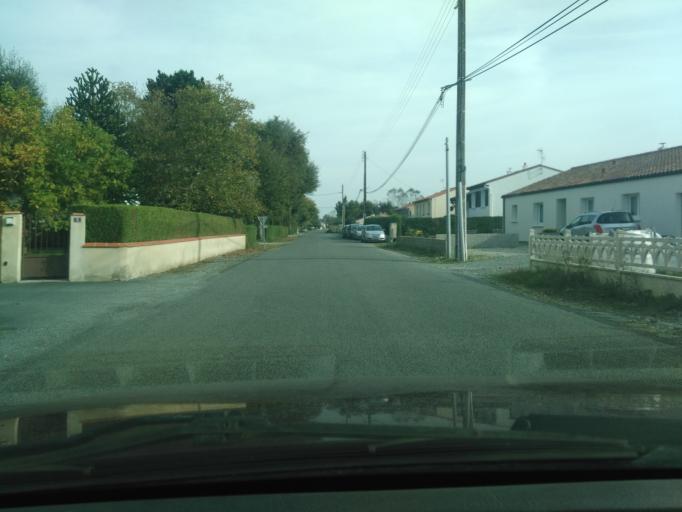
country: FR
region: Pays de la Loire
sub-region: Departement de la Vendee
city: Les Essarts
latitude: 46.7552
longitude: -1.2510
